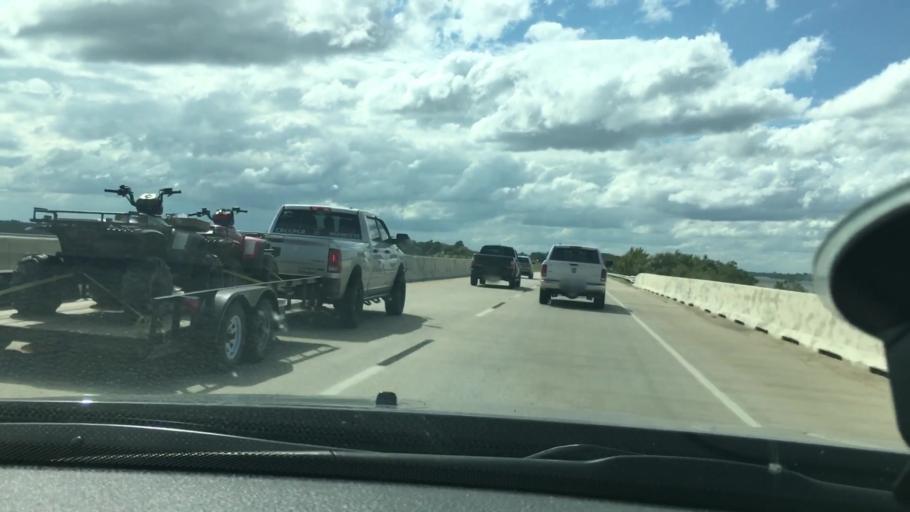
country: US
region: Oklahoma
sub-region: McIntosh County
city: Checotah
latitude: 35.4591
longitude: -95.6093
